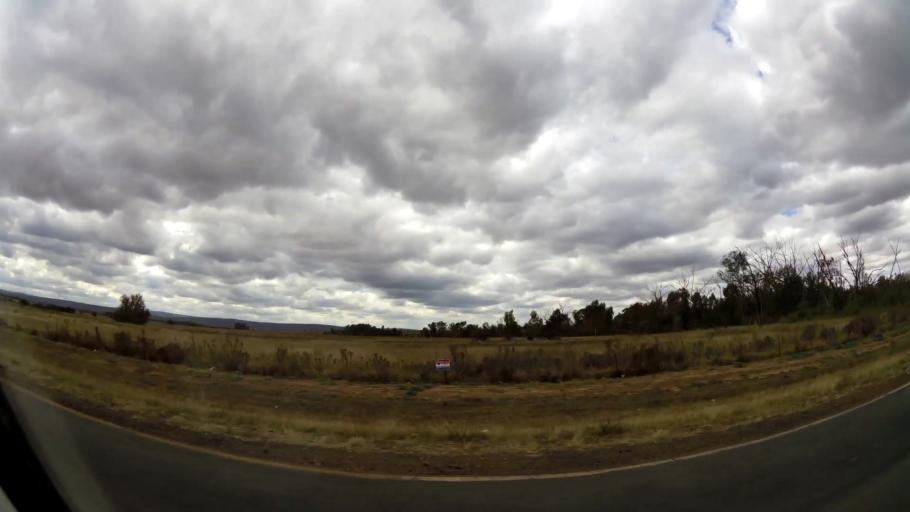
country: ZA
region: Limpopo
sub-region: Waterberg District Municipality
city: Modimolle
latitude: -24.7479
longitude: 28.4431
